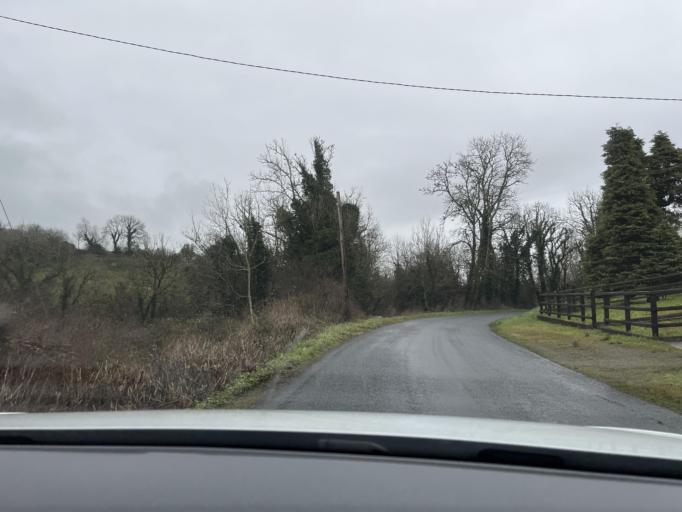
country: IE
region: Connaught
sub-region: County Leitrim
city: Manorhamilton
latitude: 54.2975
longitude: -8.0659
